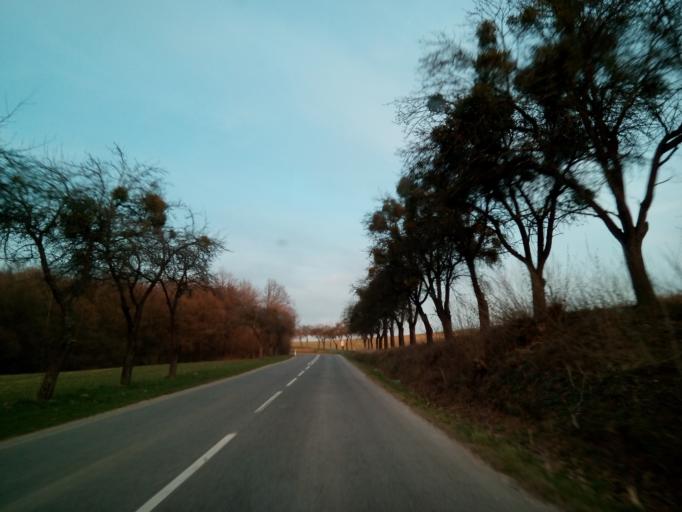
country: SK
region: Kosicky
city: Roznava
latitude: 48.6669
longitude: 20.4201
